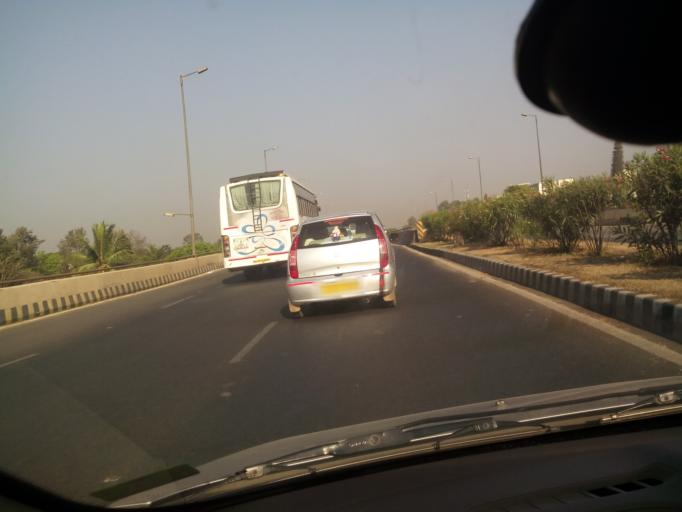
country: IN
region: Karnataka
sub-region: Bangalore Rural
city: Nelamangala
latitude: 13.0527
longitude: 77.4862
